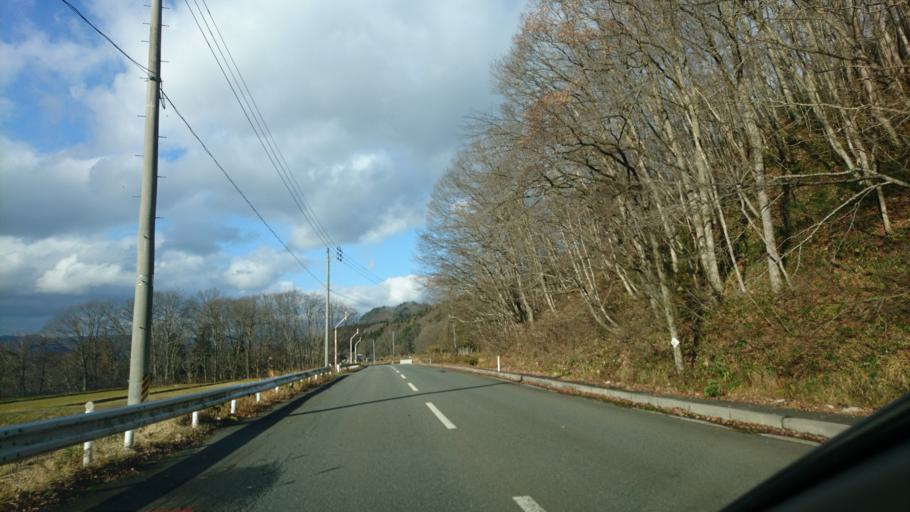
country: JP
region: Akita
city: Yokotemachi
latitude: 39.3672
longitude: 140.7710
